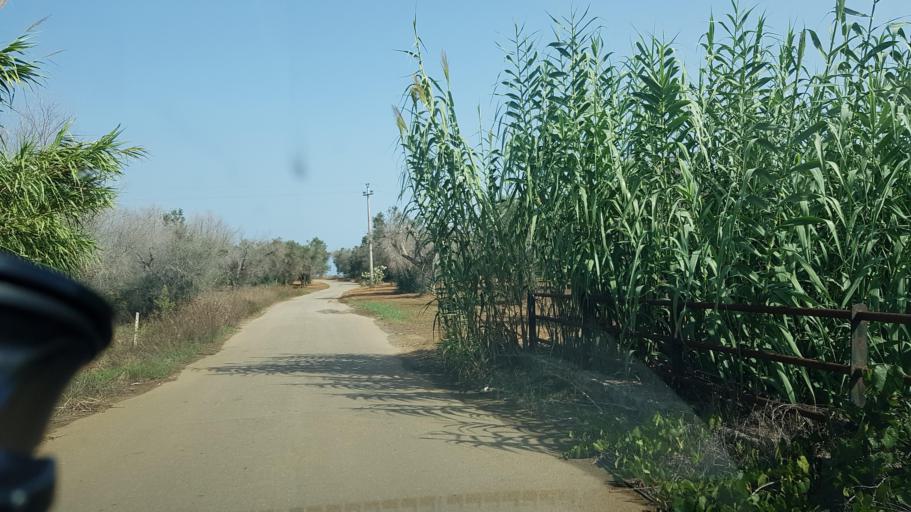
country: IT
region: Apulia
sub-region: Provincia di Brindisi
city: Torchiarolo
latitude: 40.5071
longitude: 18.0597
